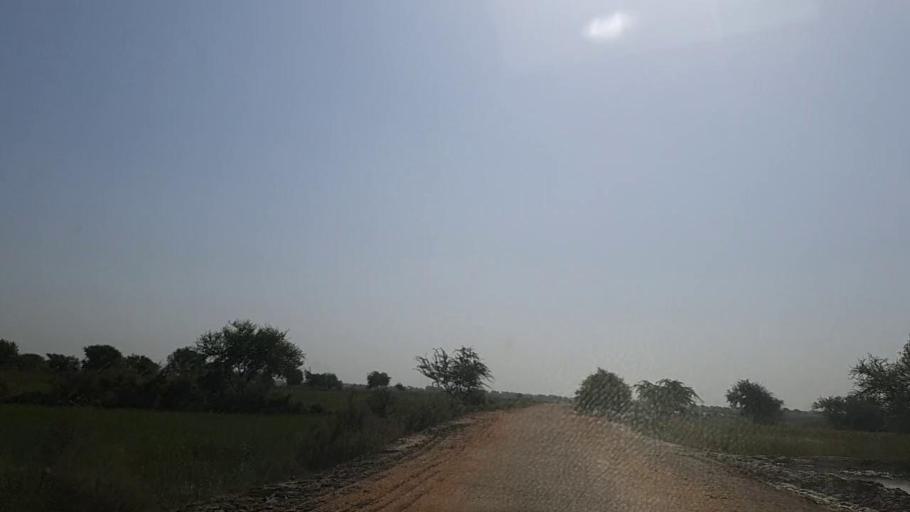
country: PK
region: Sindh
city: Daro Mehar
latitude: 24.7069
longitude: 68.1259
